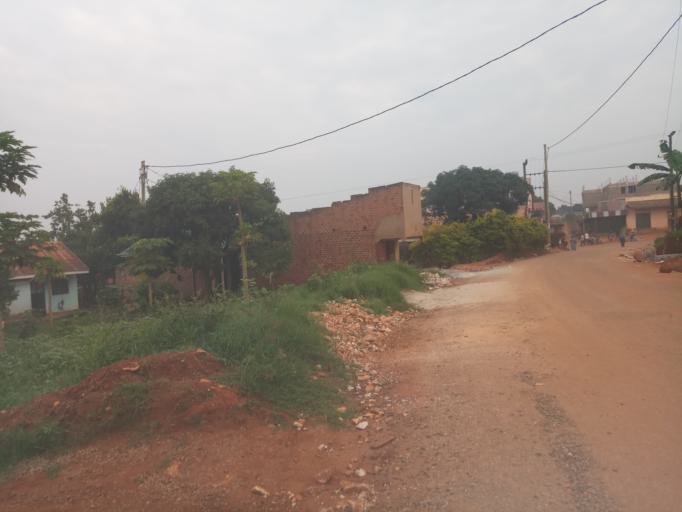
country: UG
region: Central Region
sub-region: Wakiso District
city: Kireka
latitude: 0.3942
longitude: 32.6338
